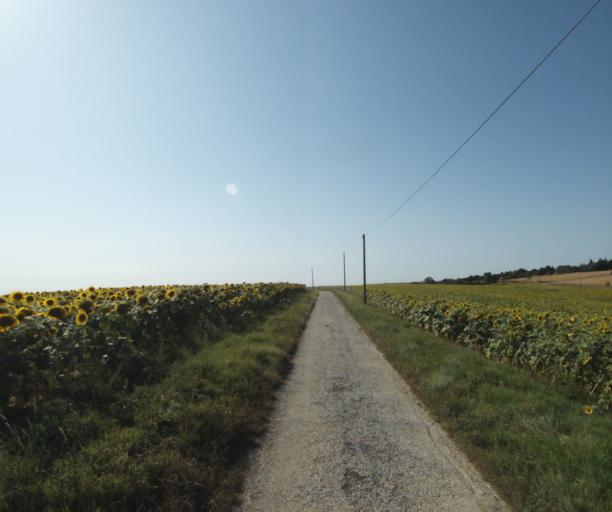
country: FR
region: Midi-Pyrenees
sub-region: Departement de la Haute-Garonne
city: Avignonet-Lauragais
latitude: 43.4196
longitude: 1.8200
